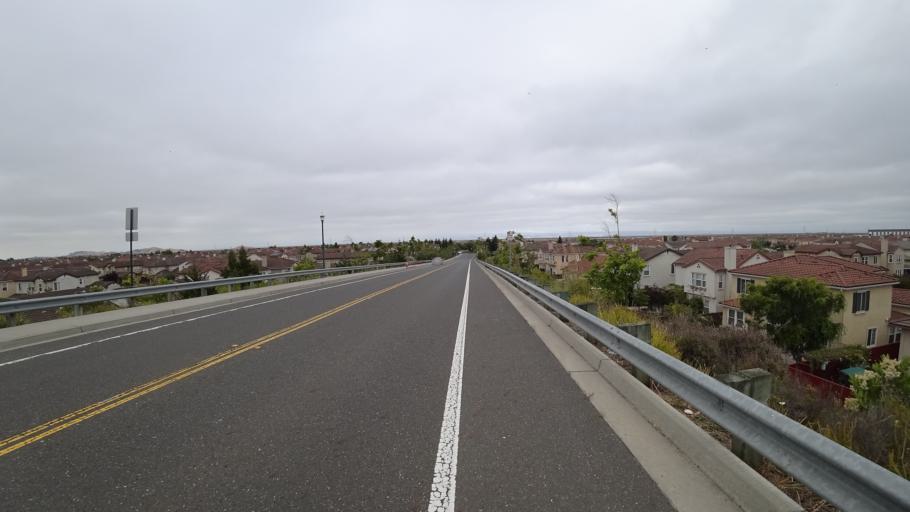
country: US
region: California
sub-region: Alameda County
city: Hayward
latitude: 37.6119
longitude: -122.0930
